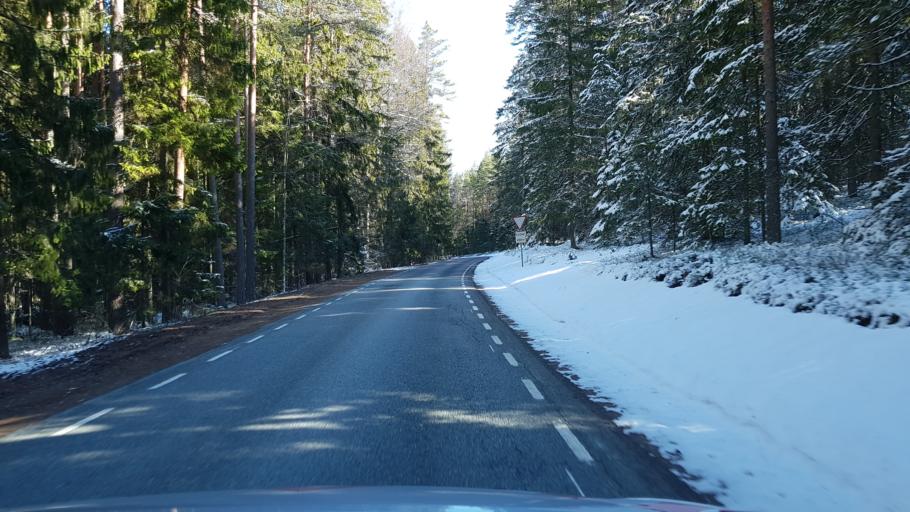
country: EE
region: Laeaene-Virumaa
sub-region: Kadrina vald
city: Kadrina
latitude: 59.5547
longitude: 25.9918
